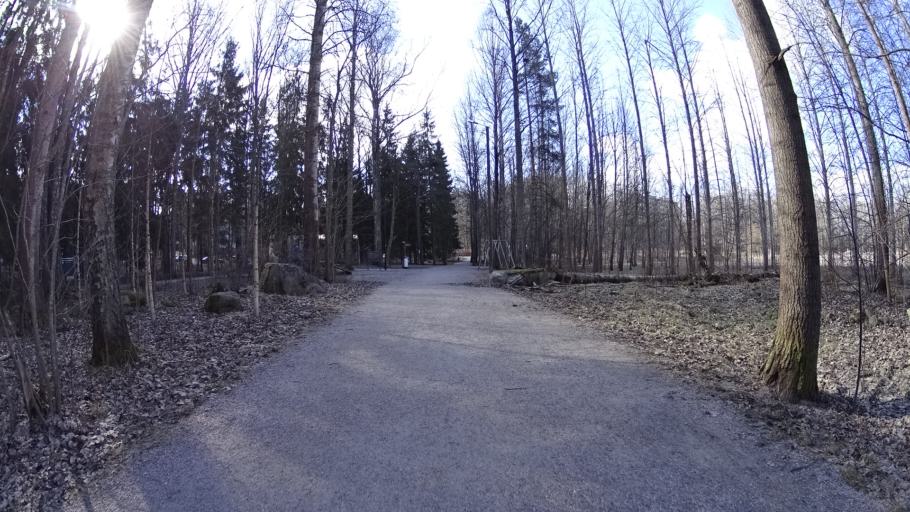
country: FI
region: Uusimaa
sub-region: Helsinki
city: Teekkarikylae
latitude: 60.2105
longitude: 24.8683
